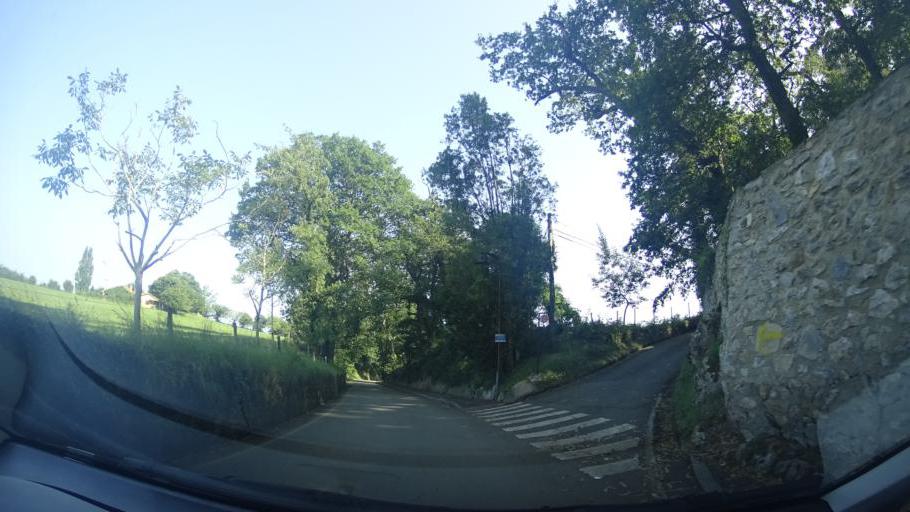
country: ES
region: Asturias
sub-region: Province of Asturias
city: Colunga
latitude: 43.4651
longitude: -5.1875
